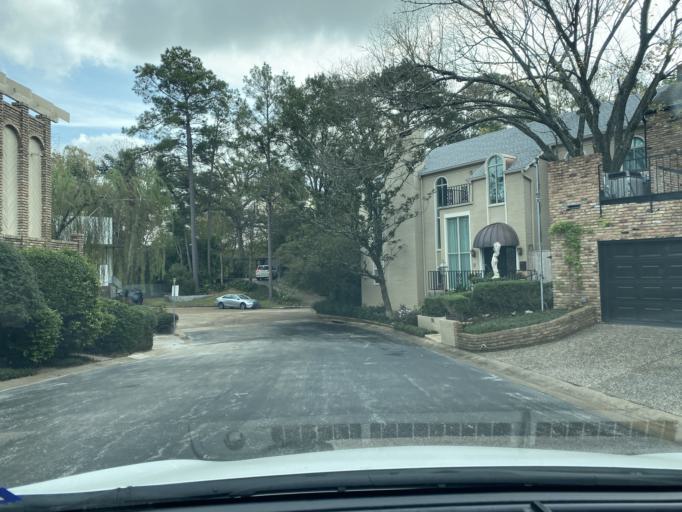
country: US
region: Texas
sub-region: Harris County
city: Hunters Creek Village
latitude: 29.7680
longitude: -95.4665
